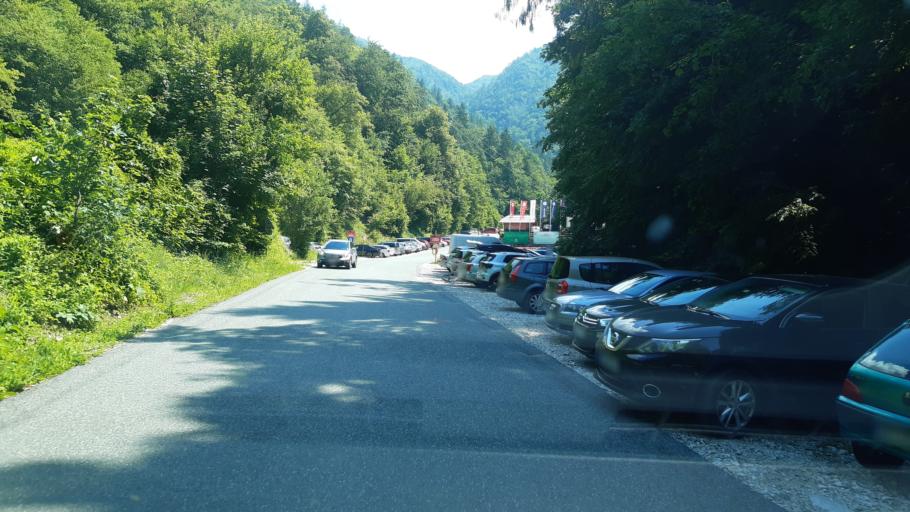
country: SI
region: Cerklje na Gorenjskem
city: Cerklje na Gorenjskem
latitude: 46.2847
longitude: 14.4961
